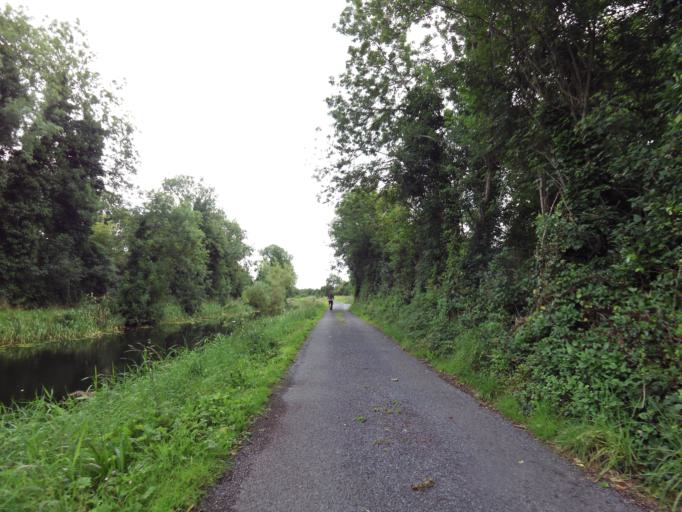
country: IE
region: Leinster
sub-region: An Iarmhi
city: An Muileann gCearr
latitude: 53.5459
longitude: -7.4738
